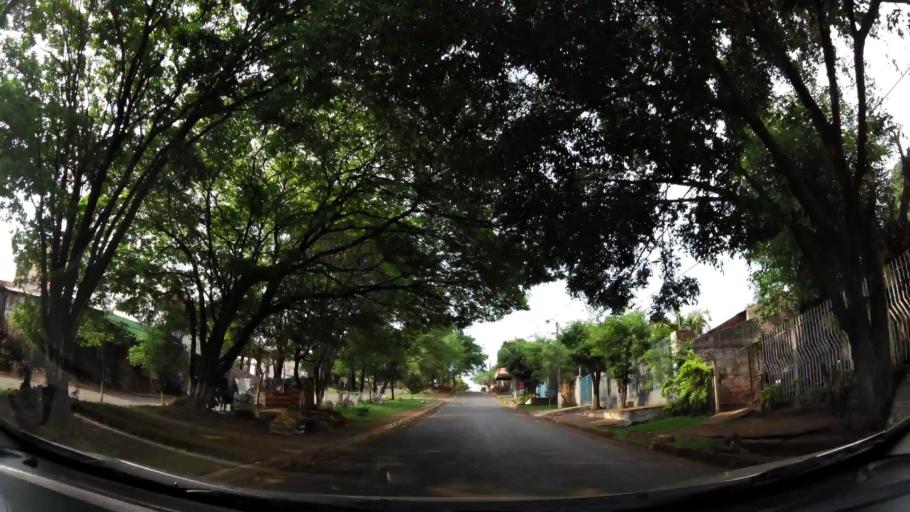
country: PY
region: Alto Parana
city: Ciudad del Este
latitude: -25.4918
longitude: -54.6484
